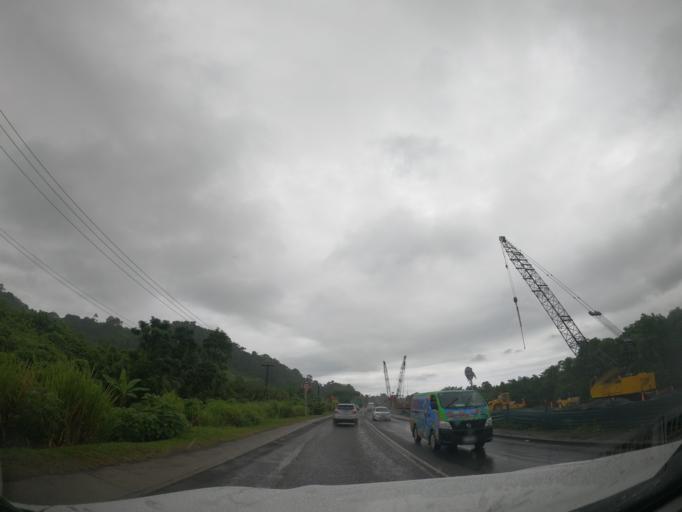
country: FJ
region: Central
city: Suva
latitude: -18.1140
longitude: 178.4309
